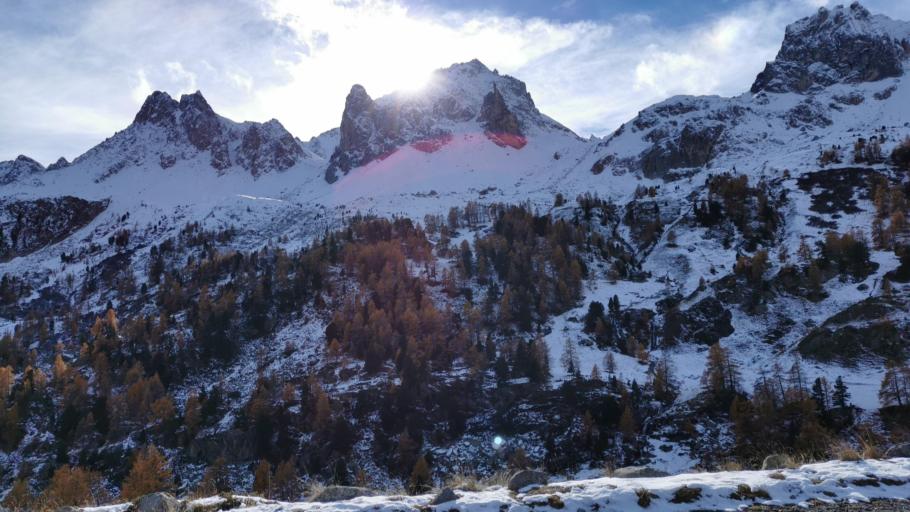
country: FR
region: Provence-Alpes-Cote d'Azur
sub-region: Departement des Hautes-Alpes
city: Le Monetier-les-Bains
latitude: 45.0667
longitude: 6.5191
